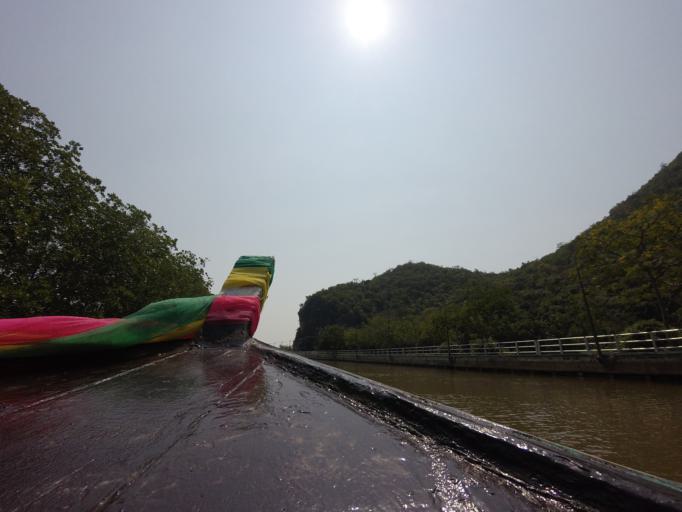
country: TH
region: Prachuap Khiri Khan
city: Kui Buri
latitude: 12.1350
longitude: 99.9619
